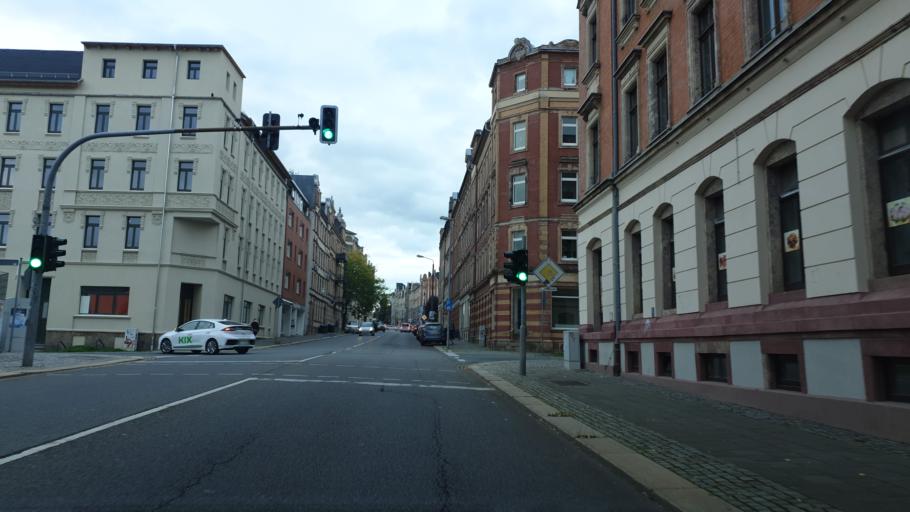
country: DE
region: Saxony
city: Chemnitz
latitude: 50.8362
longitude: 12.9365
